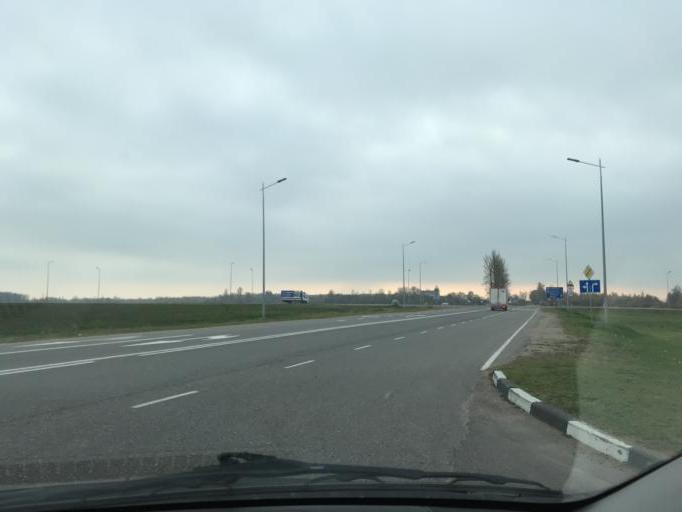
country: BY
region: Vitebsk
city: Chashniki
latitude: 55.0175
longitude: 29.4405
